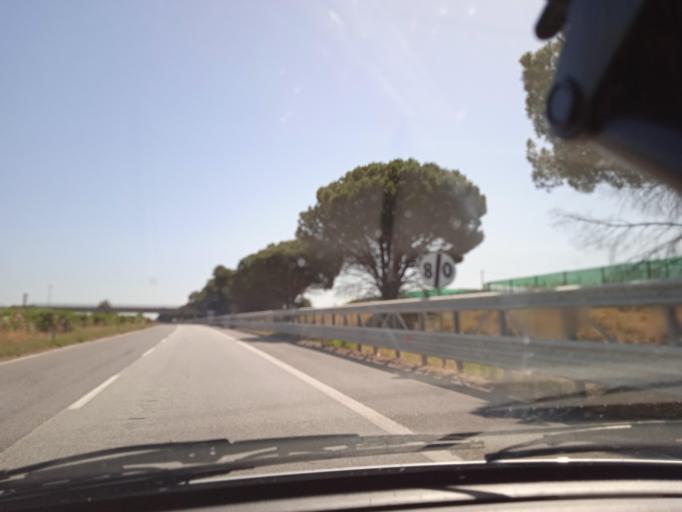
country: IT
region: Sicily
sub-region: Messina
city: Meri
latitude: 38.1839
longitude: 15.2578
